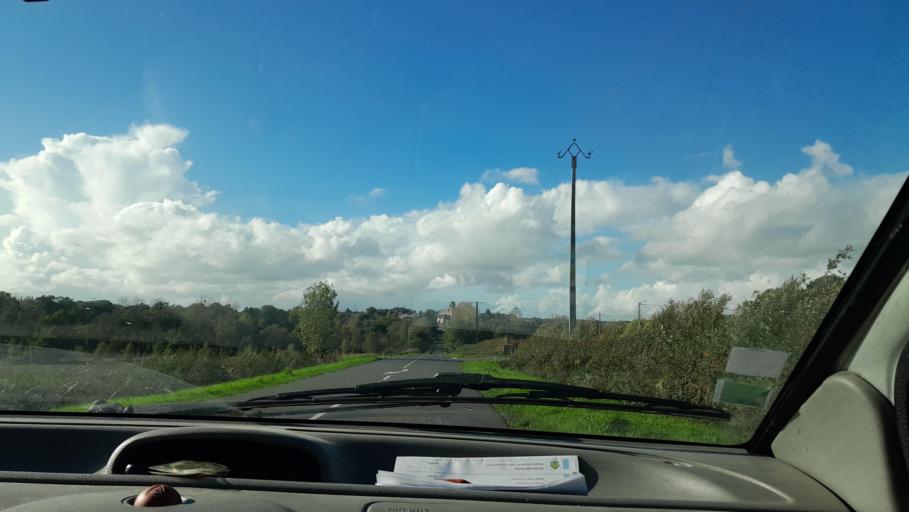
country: FR
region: Pays de la Loire
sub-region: Departement de la Mayenne
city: Cosse-le-Vivien
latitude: 47.9573
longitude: -0.9682
